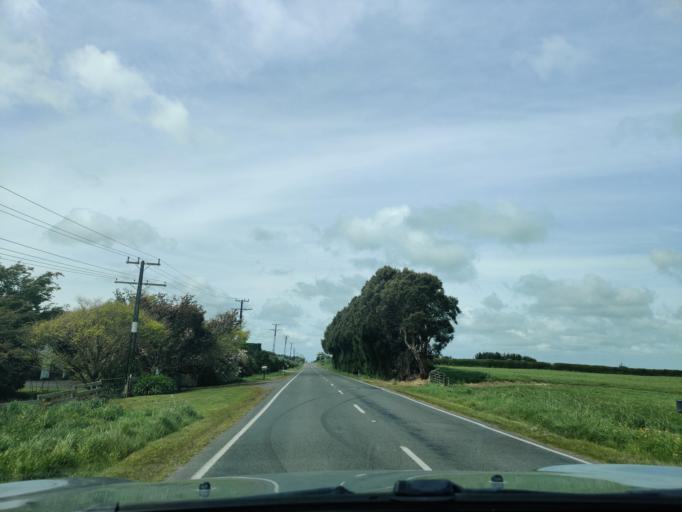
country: NZ
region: Taranaki
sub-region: South Taranaki District
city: Eltham
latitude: -39.4283
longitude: 174.1602
